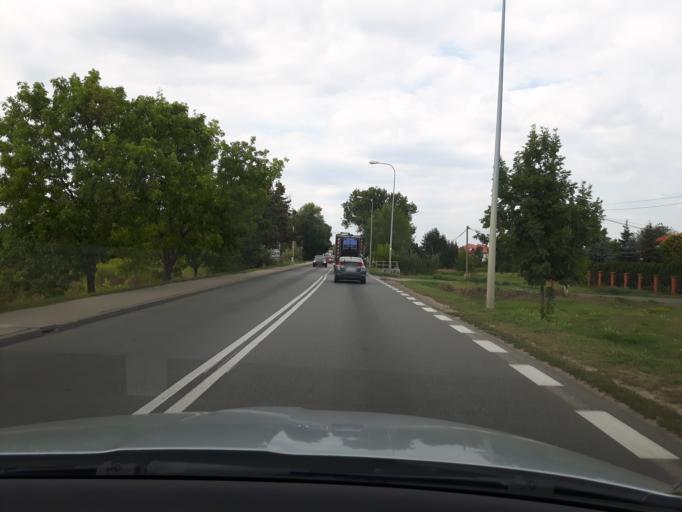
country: PL
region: Masovian Voivodeship
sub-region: Powiat legionowski
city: Stanislawow Pierwszy
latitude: 52.3524
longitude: 21.0294
